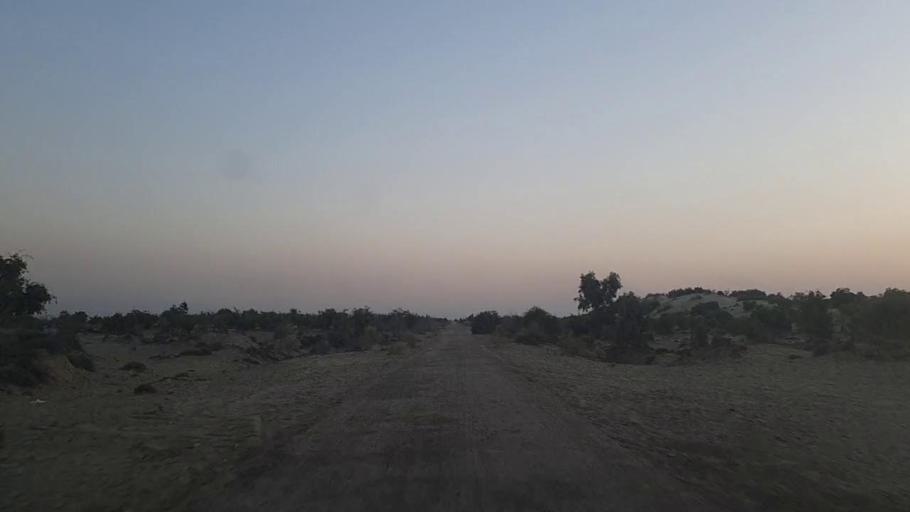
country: PK
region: Sindh
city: Jam Sahib
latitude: 26.4130
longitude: 68.8094
